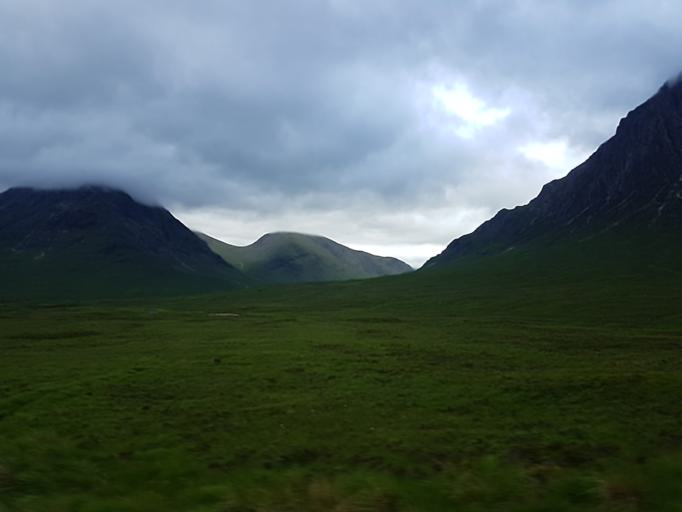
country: GB
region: Scotland
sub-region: Highland
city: Spean Bridge
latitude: 56.6560
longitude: -4.8686
